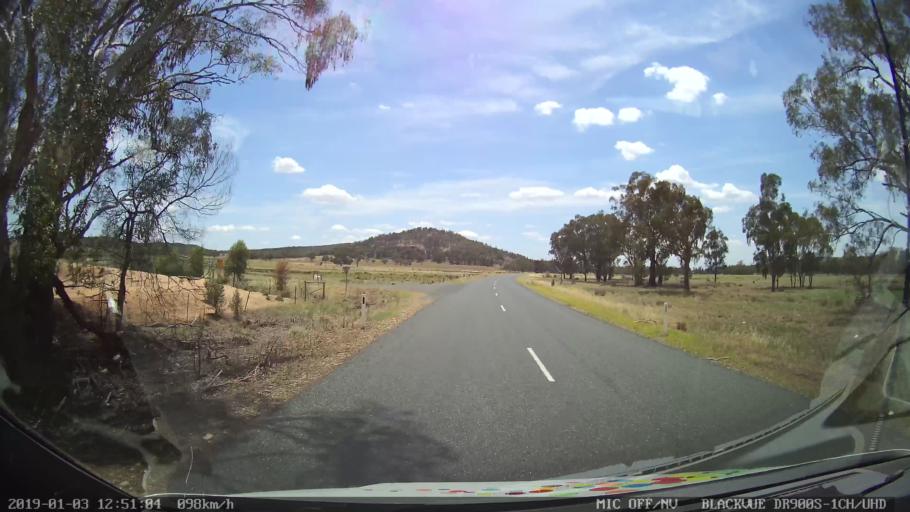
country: AU
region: New South Wales
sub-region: Weddin
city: Grenfell
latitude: -33.6837
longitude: 148.2763
